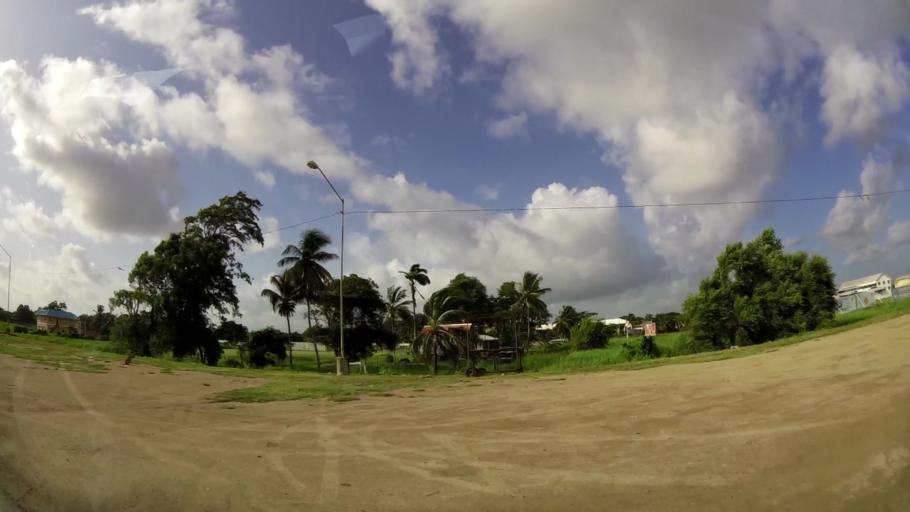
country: GY
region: Demerara-Mahaica
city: Georgetown
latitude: 6.8247
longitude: -58.1549
